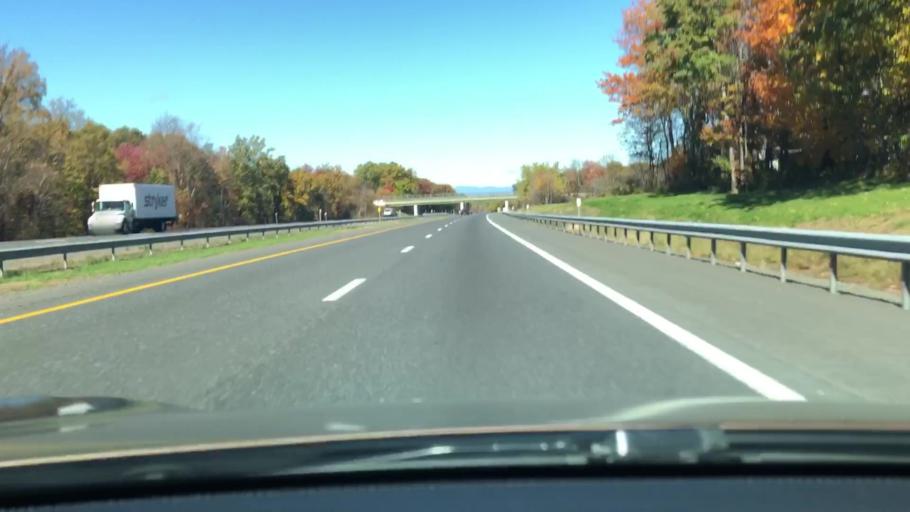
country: US
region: New York
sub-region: Ulster County
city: Plattekill
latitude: 41.6584
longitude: -74.0782
